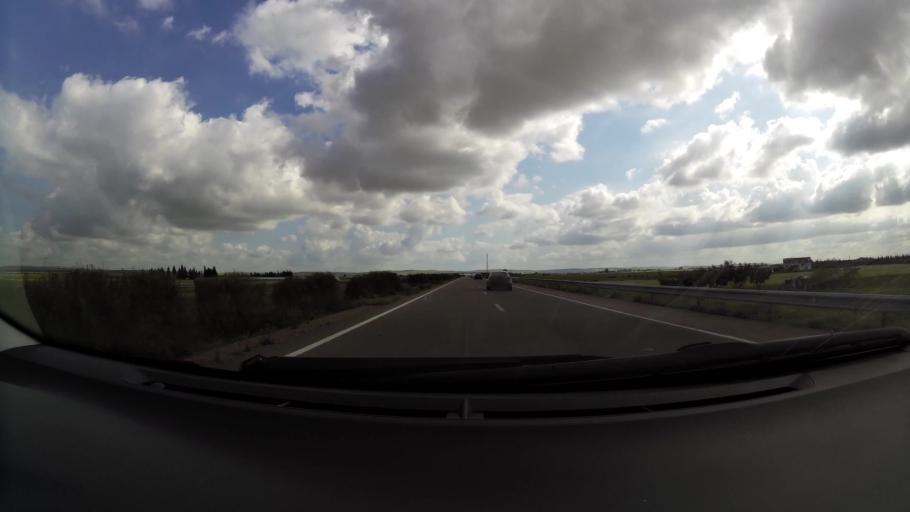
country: MA
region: Chaouia-Ouardigha
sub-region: Settat Province
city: Berrechid
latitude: 33.1430
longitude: -7.5748
